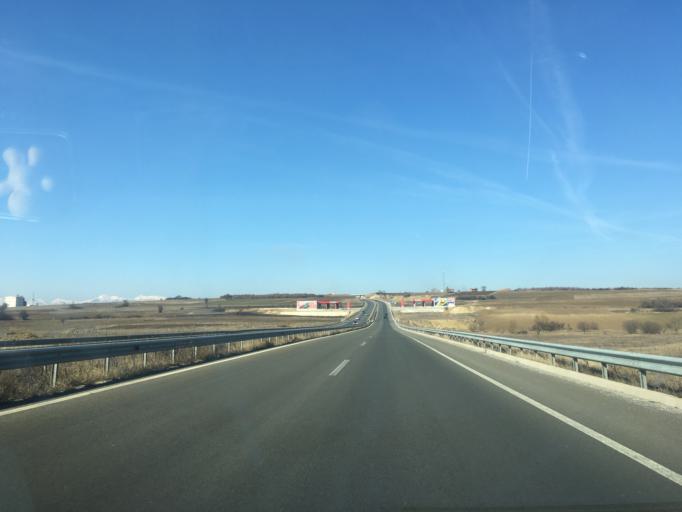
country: XK
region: Prizren
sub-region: Komuna e Malisheves
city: Llazice
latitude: 42.5712
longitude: 20.7327
